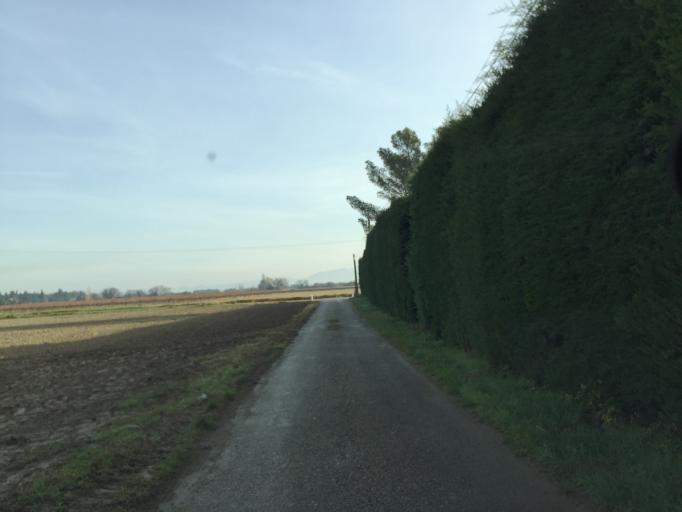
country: FR
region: Provence-Alpes-Cote d'Azur
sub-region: Departement du Vaucluse
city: Serignan-du-Comtat
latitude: 44.1639
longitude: 4.8378
